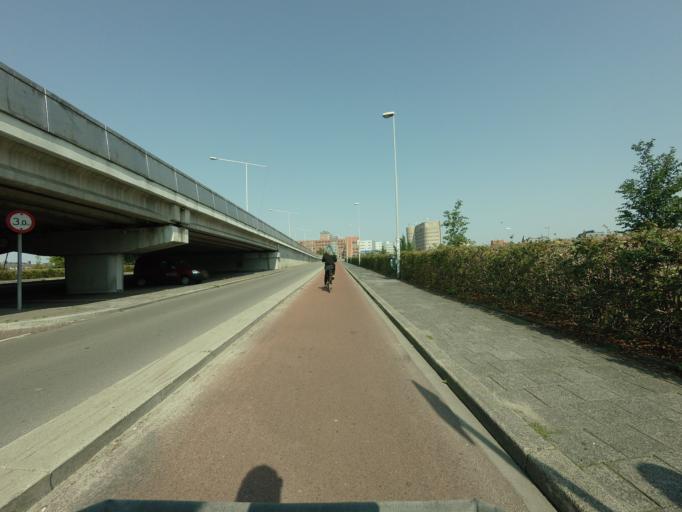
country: NL
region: Groningen
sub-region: Gemeente Groningen
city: Groningen
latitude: 53.2080
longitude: 6.5620
